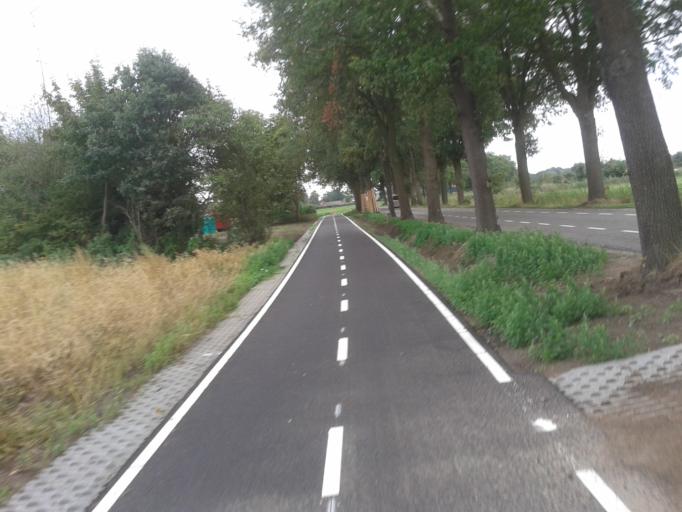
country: NL
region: North Brabant
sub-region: Gemeente Hilvarenbeek
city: Hilvarenbeek
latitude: 51.5128
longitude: 5.1955
